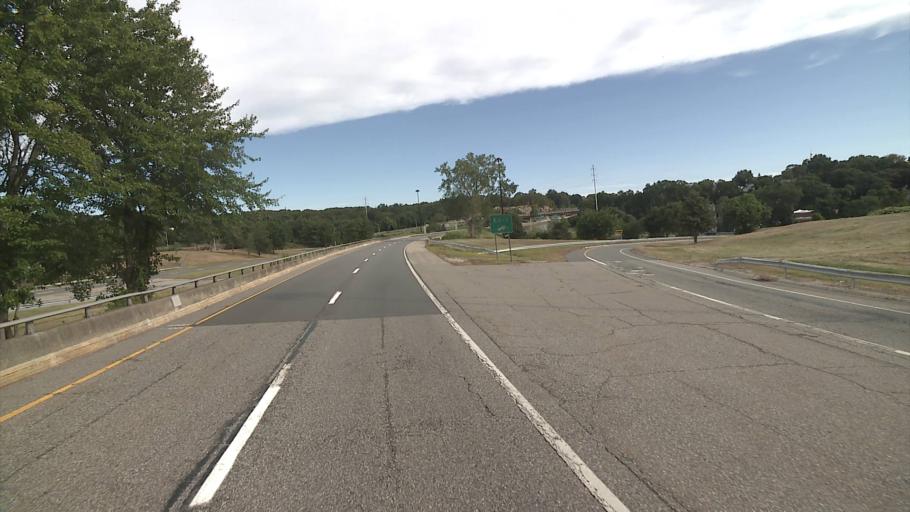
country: US
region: Connecticut
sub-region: New London County
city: New London
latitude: 41.3661
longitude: -72.1057
